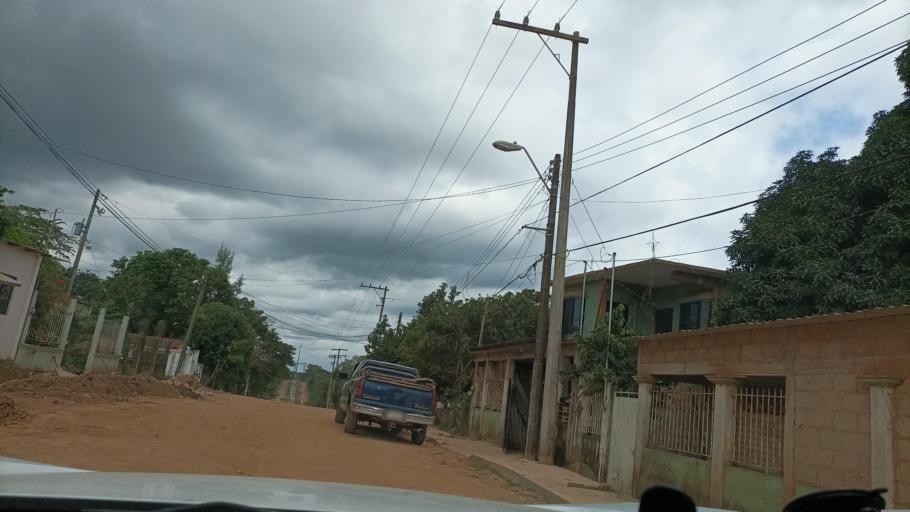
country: MX
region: Veracruz
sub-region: Soconusco
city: Colonia Lealtad
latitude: 17.9630
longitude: -94.8961
